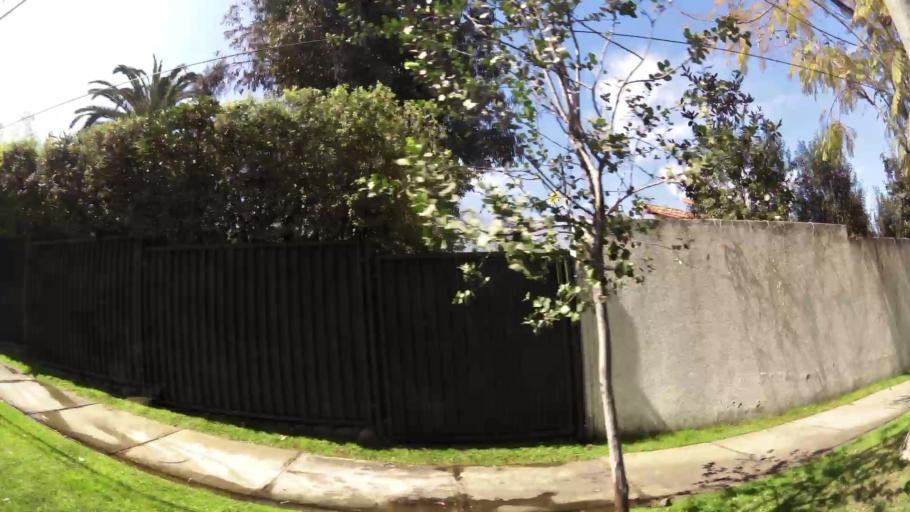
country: CL
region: Santiago Metropolitan
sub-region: Provincia de Santiago
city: Villa Presidente Frei, Nunoa, Santiago, Chile
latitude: -33.4455
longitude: -70.5271
